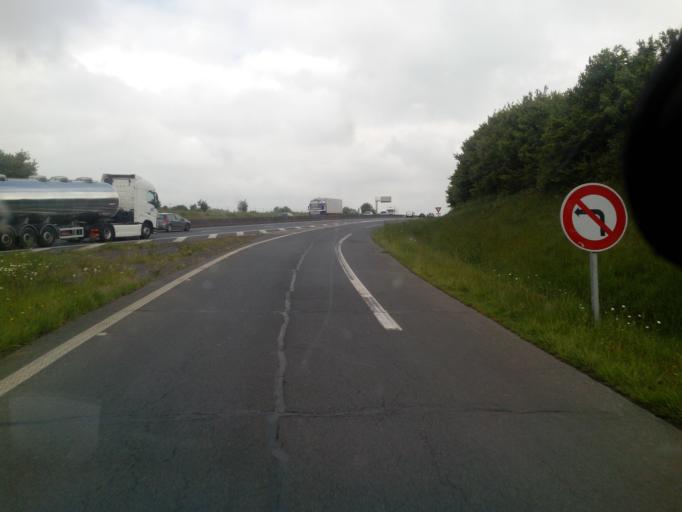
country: FR
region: Lower Normandy
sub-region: Departement du Calvados
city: Villers-Bocage
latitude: 49.0683
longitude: -0.6559
